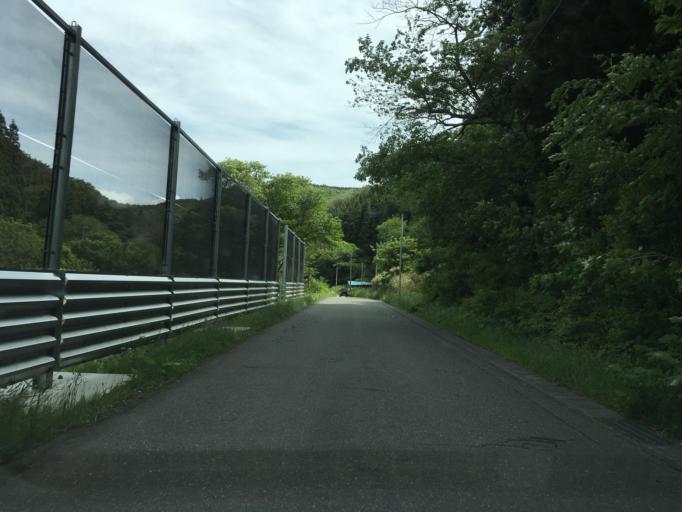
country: JP
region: Iwate
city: Mizusawa
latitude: 39.1017
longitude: 141.3344
